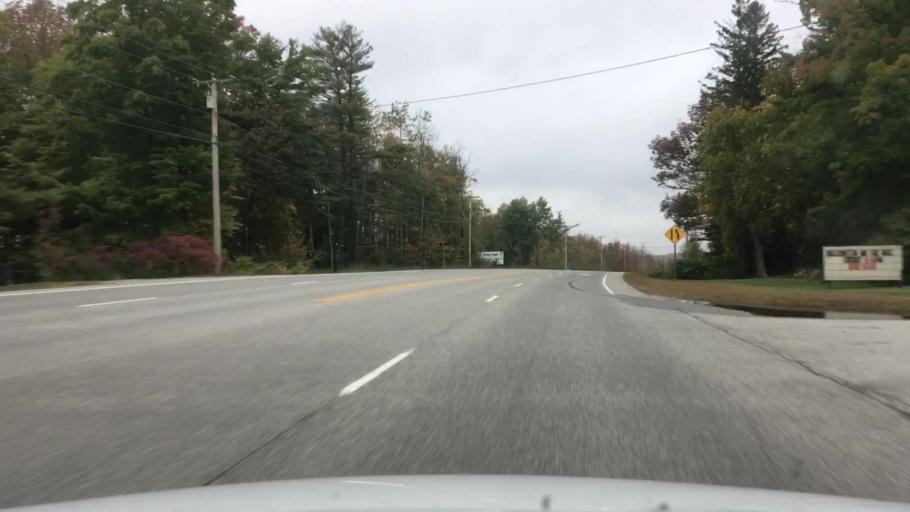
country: US
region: Maine
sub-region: Androscoggin County
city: Poland
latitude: 44.0246
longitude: -70.3656
